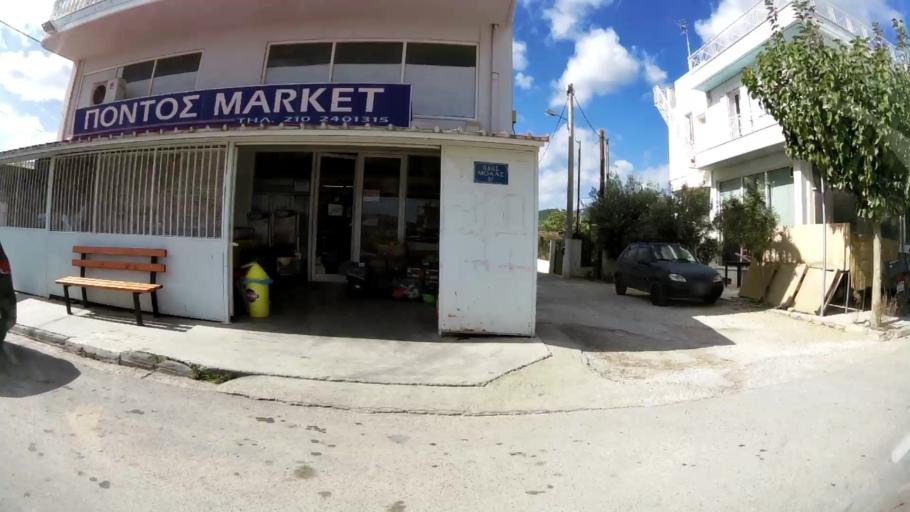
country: GR
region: Attica
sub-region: Nomarchia Anatolikis Attikis
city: Acharnes
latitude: 38.1040
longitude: 23.7500
